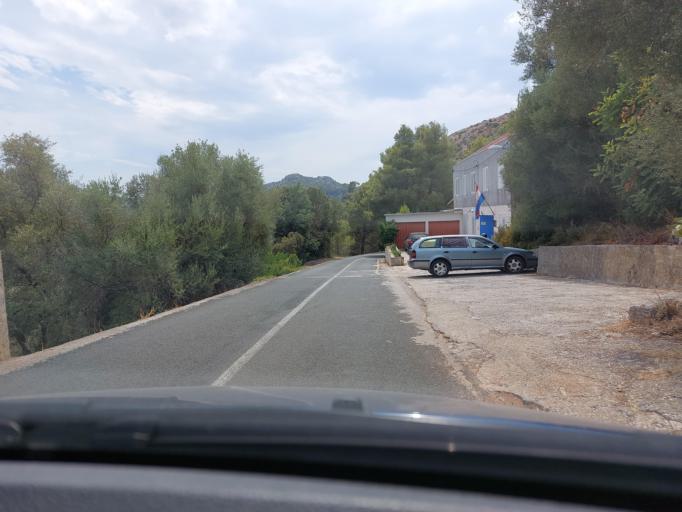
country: HR
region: Dubrovacko-Neretvanska
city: Smokvica
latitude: 42.7666
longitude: 16.8932
